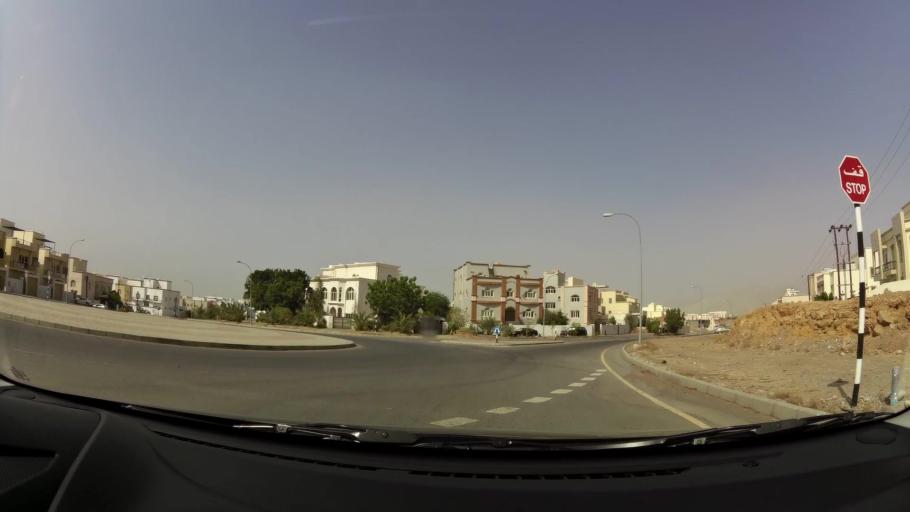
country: OM
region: Muhafazat Masqat
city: Bawshar
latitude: 23.5510
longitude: 58.3488
